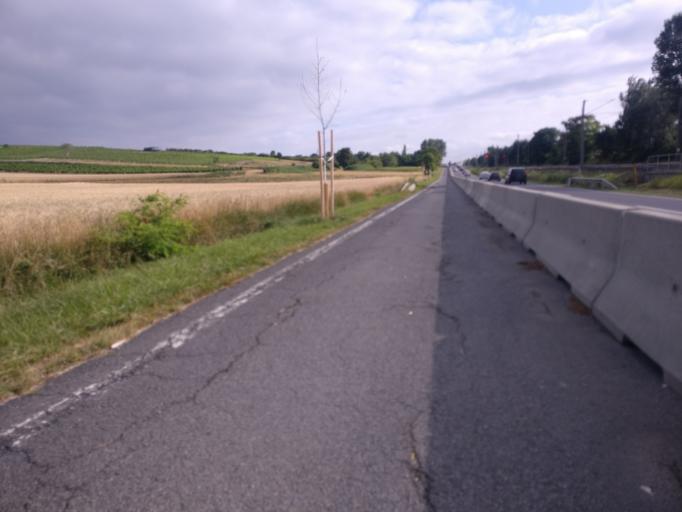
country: AT
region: Lower Austria
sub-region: Politischer Bezirk Modling
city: Neu-Guntramsdorf
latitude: 48.0582
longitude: 16.3106
